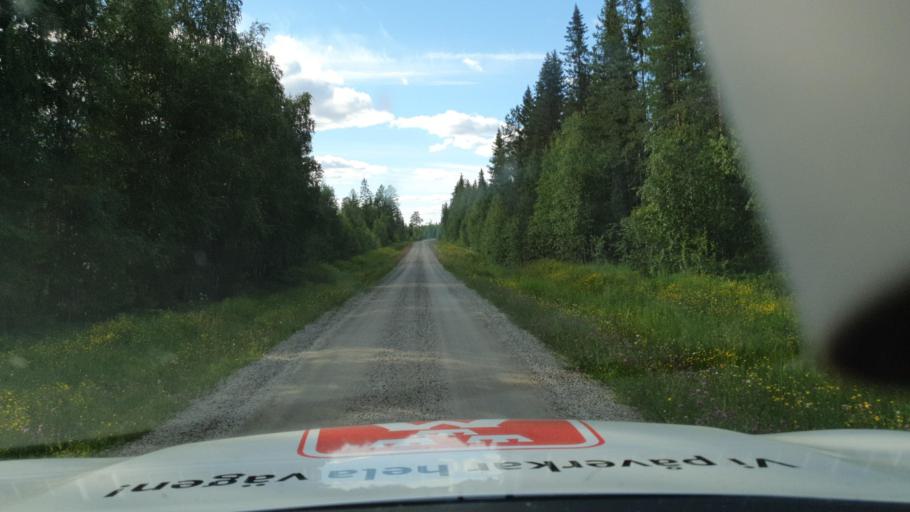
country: SE
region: Vaesterbotten
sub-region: Lycksele Kommun
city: Lycksele
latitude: 64.4701
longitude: 18.2904
